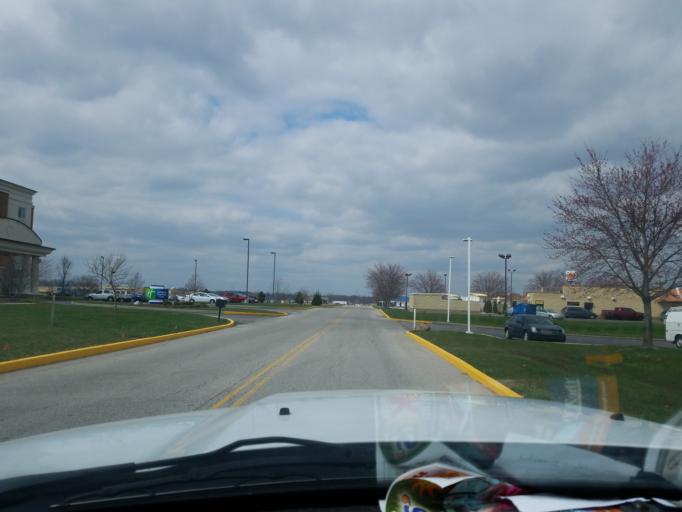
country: US
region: Indiana
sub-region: Vigo County
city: Terre Haute
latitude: 39.4340
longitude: -87.3342
